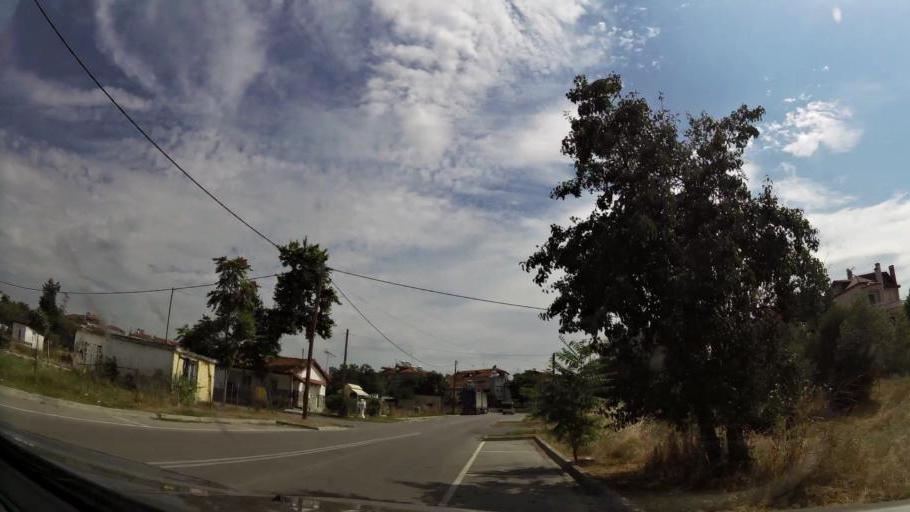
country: GR
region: Central Macedonia
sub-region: Nomos Pierias
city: Katerini
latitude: 40.2674
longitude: 22.4904
